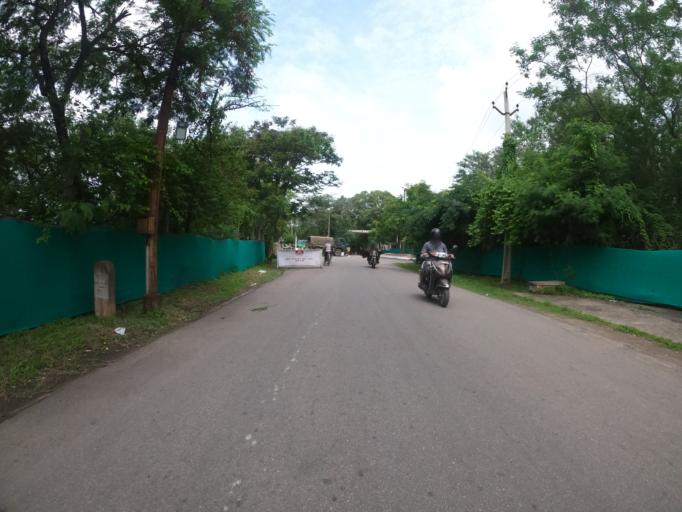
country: IN
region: Telangana
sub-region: Hyderabad
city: Hyderabad
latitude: 17.3915
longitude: 78.4201
